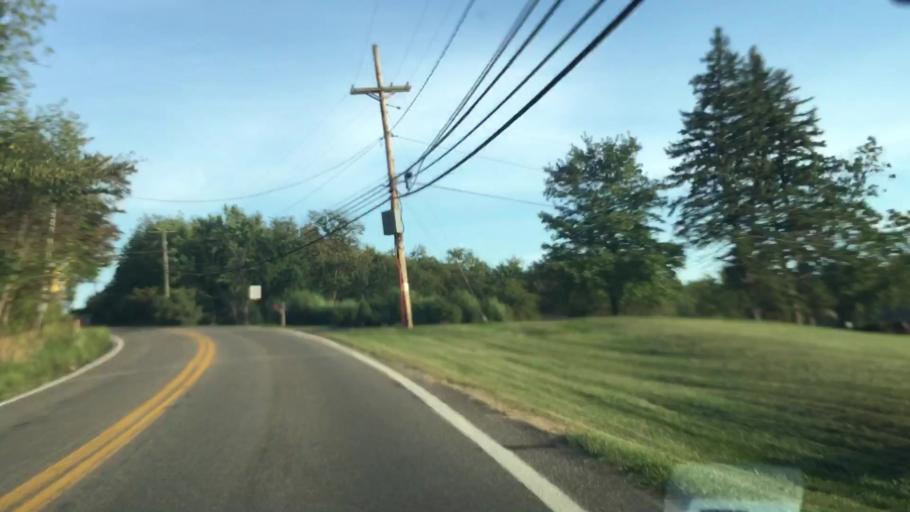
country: US
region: Pennsylvania
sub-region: Beaver County
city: Ambridge
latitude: 40.5767
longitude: -80.2789
